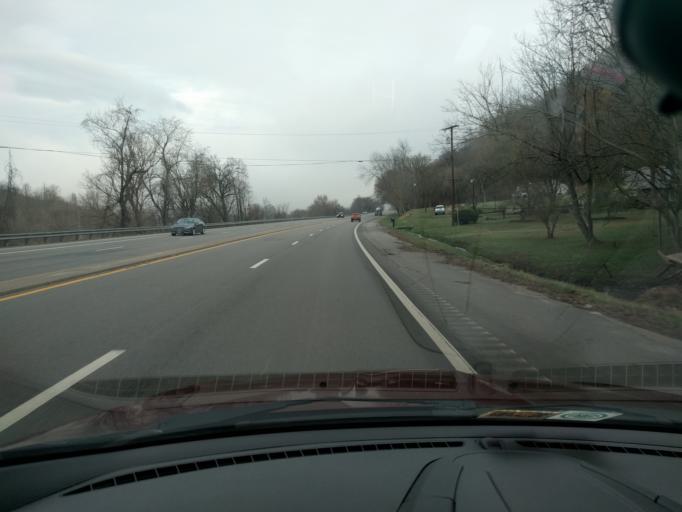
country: US
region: West Virginia
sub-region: Kanawha County
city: Marmet
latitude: 38.2585
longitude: -81.5653
